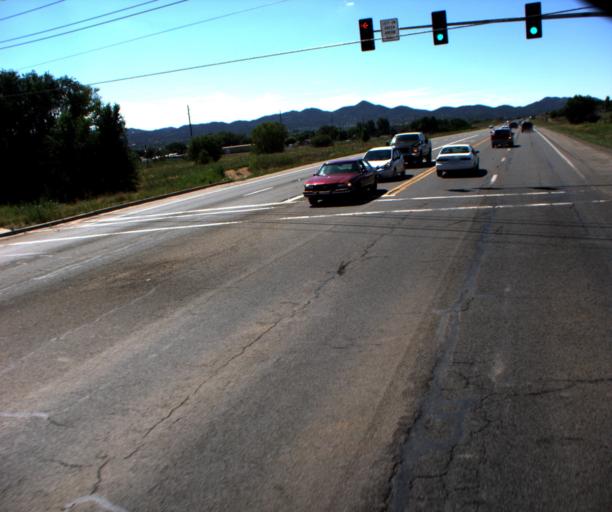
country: US
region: Arizona
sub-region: Yavapai County
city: Dewey-Humboldt
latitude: 34.5391
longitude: -112.2464
